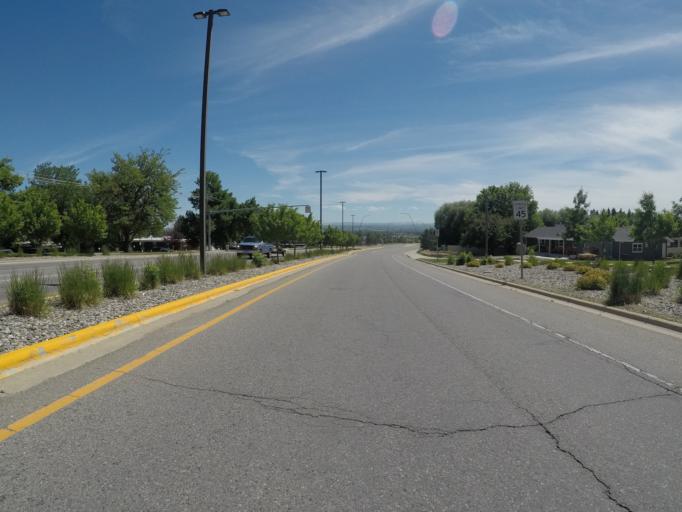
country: US
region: Montana
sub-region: Yellowstone County
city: Billings
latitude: 45.7981
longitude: -108.6179
